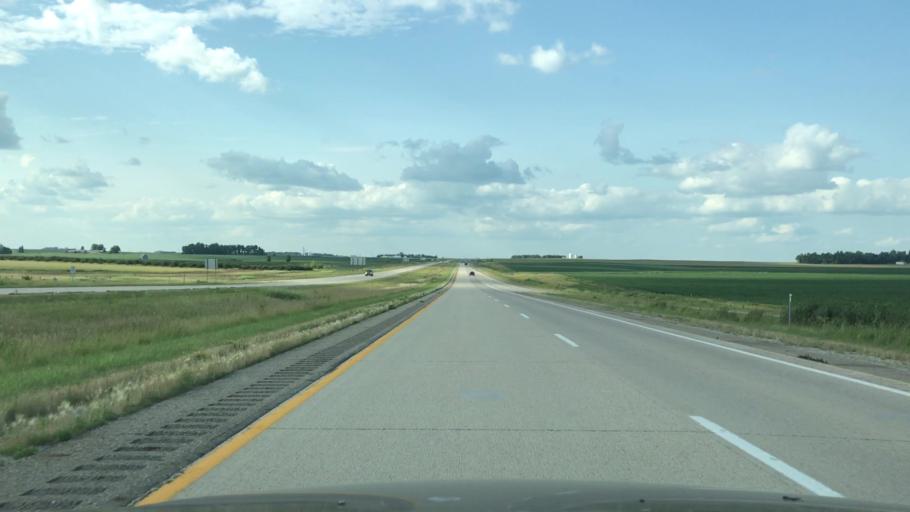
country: US
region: Iowa
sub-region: Osceola County
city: Sibley
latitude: 43.4357
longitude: -95.7133
